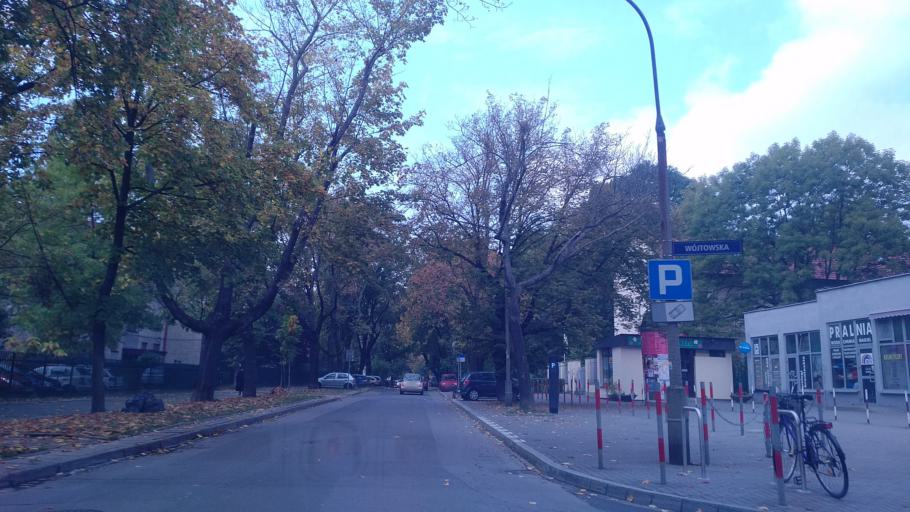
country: PL
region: Lesser Poland Voivodeship
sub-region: Krakow
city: Krakow
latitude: 50.0750
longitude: 19.9263
